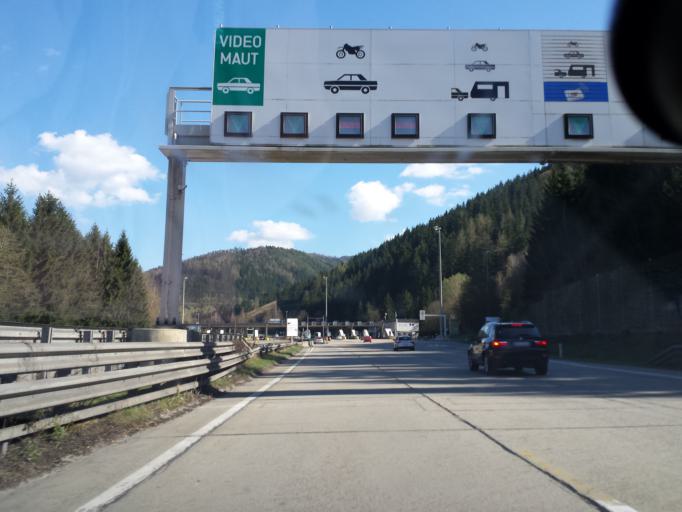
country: AT
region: Styria
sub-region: Politischer Bezirk Leoben
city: Sankt Michael in Obersteiermark
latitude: 47.3252
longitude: 15.0280
